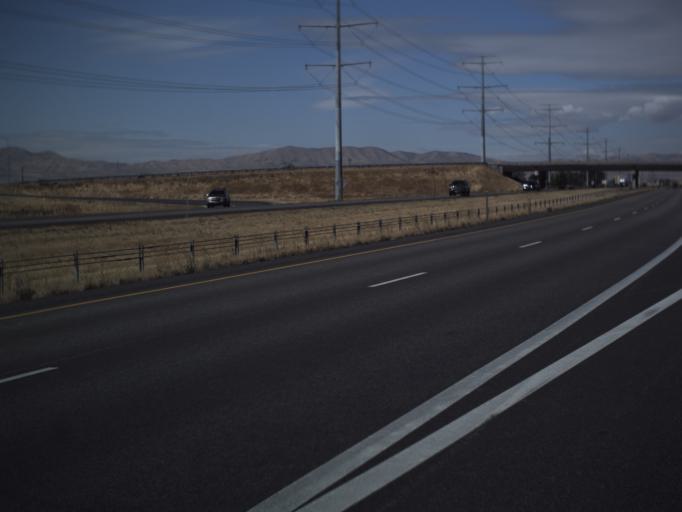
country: US
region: Utah
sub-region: Box Elder County
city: Elwood
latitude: 41.6781
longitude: -112.1370
